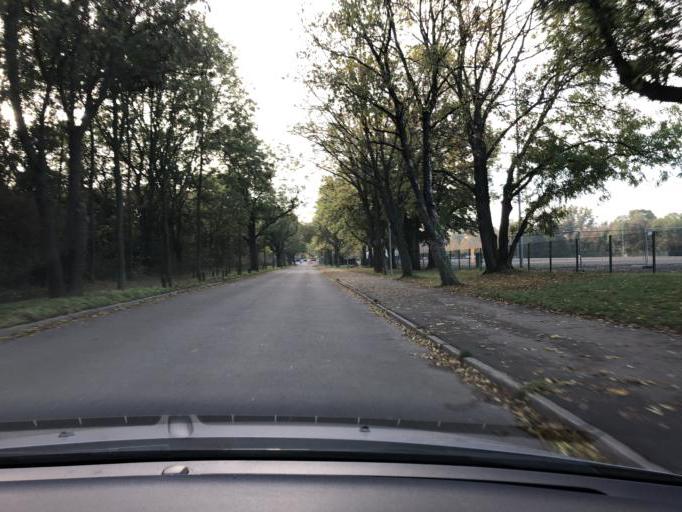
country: DE
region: Saxony
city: Leipzig
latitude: 51.3421
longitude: 12.3433
